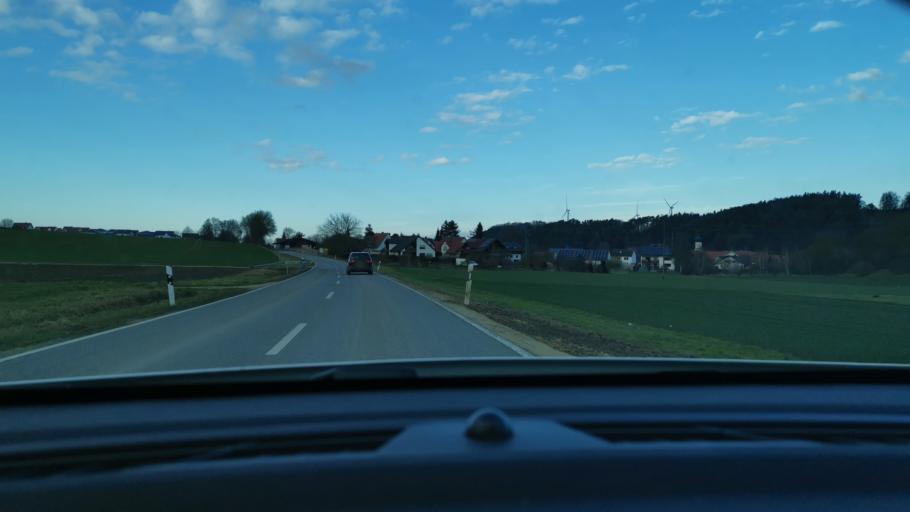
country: DE
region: Bavaria
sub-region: Swabia
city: Holzheim
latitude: 48.5805
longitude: 10.9650
